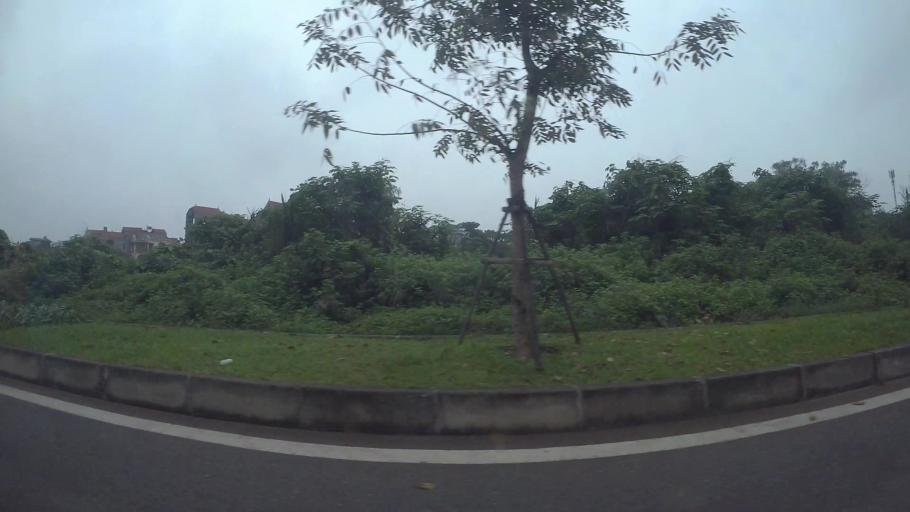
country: VN
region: Ha Noi
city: Van Dien
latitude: 20.9690
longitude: 105.8745
